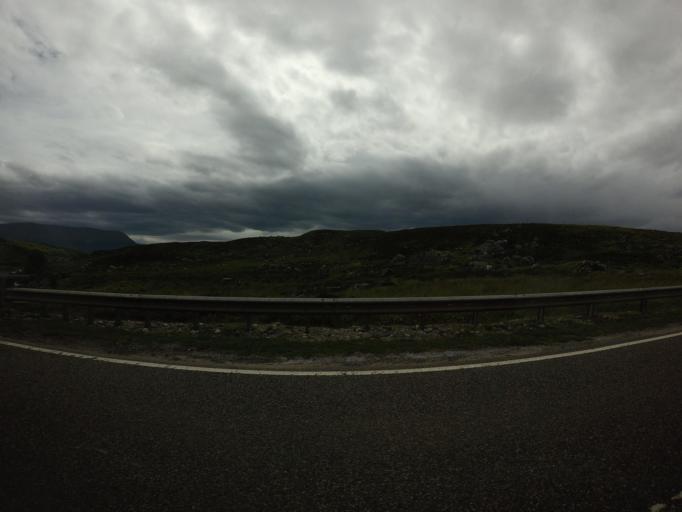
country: GB
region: Scotland
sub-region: Highland
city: Dingwall
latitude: 57.6972
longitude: -4.7321
